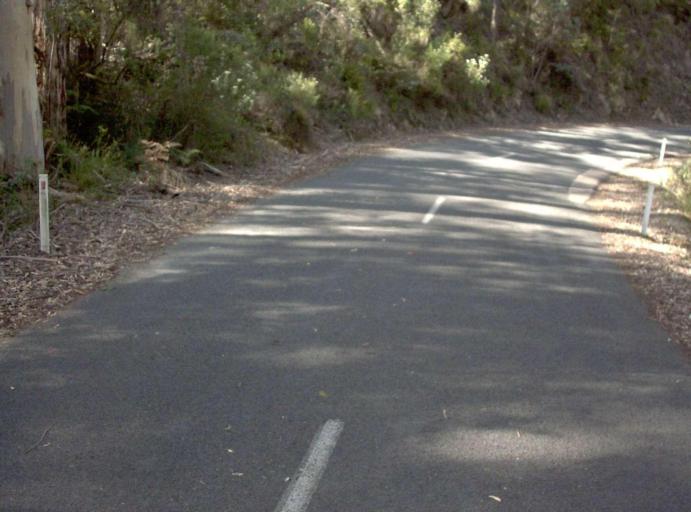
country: AU
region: Victoria
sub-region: East Gippsland
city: Lakes Entrance
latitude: -37.4549
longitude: 148.5759
